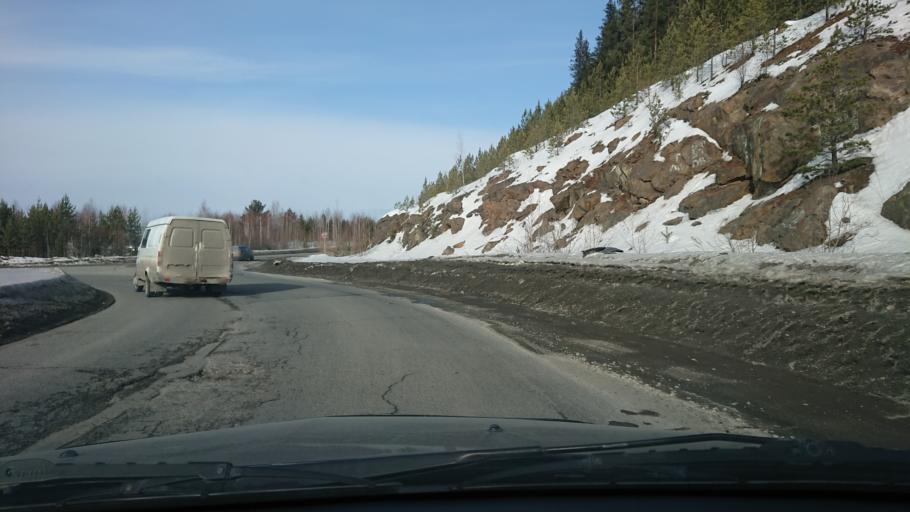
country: RU
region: Sverdlovsk
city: Revda
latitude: 56.7968
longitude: 59.9858
